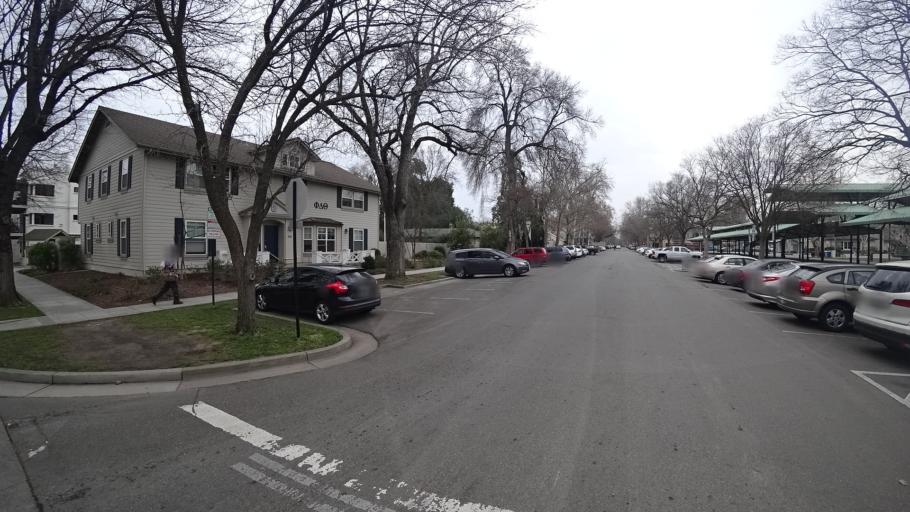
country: US
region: California
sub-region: Yolo County
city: Davis
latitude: 38.5454
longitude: -121.7440
